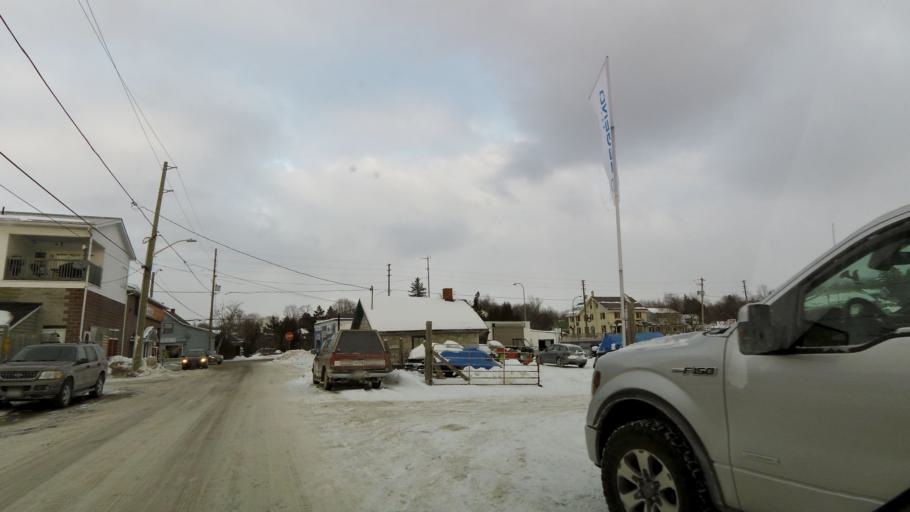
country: CA
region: Ontario
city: Omemee
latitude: 44.6583
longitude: -78.7979
